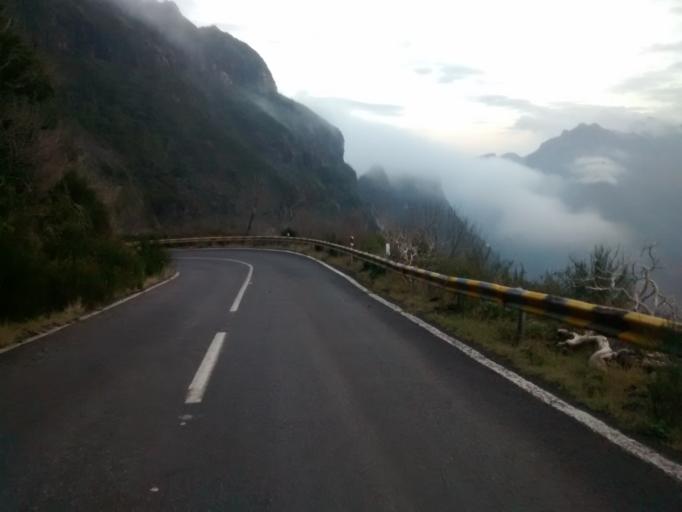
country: PT
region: Madeira
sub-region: Sao Vicente
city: Sao Vicente
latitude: 32.7436
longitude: -17.0437
